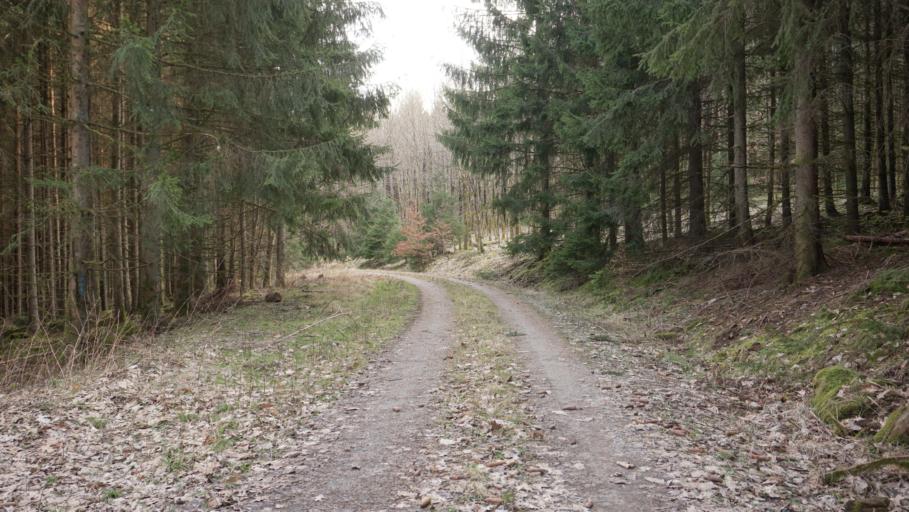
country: DE
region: Baden-Wuerttemberg
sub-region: Karlsruhe Region
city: Fahrenbach
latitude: 49.4472
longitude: 9.1236
